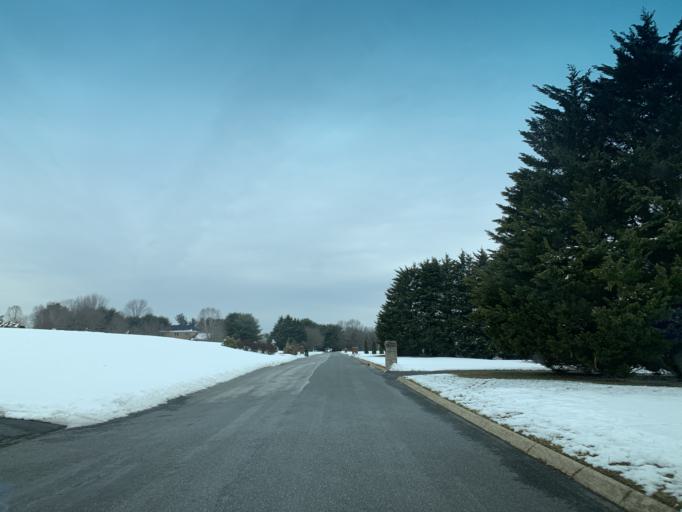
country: US
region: Maryland
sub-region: Harford County
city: Jarrettsville
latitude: 39.5840
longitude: -76.4661
